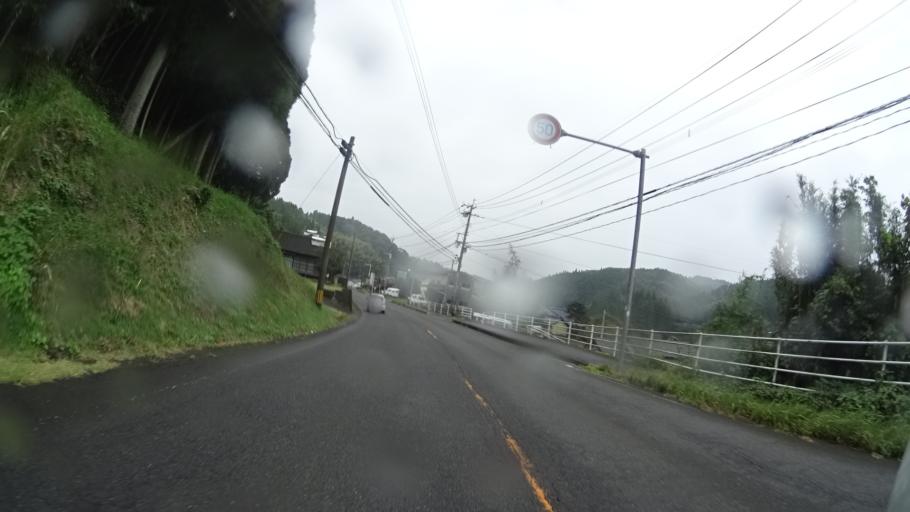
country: JP
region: Kagoshima
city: Kajiki
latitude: 31.8160
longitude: 130.6764
